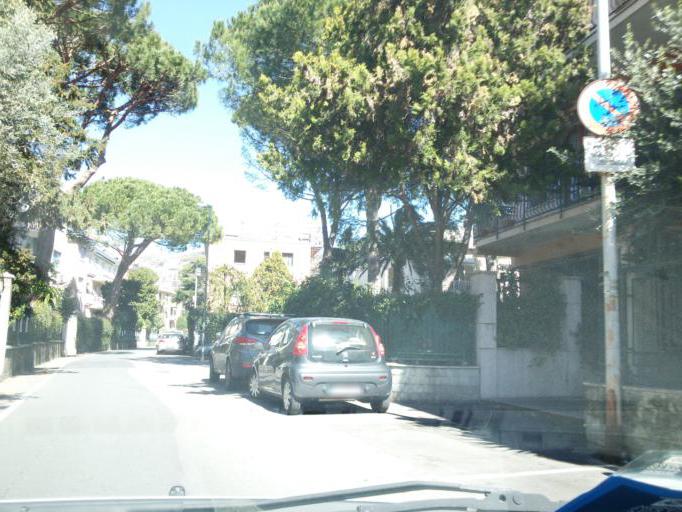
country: IT
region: Liguria
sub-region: Provincia di Genova
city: Bogliasco
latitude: 44.3892
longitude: 9.0013
